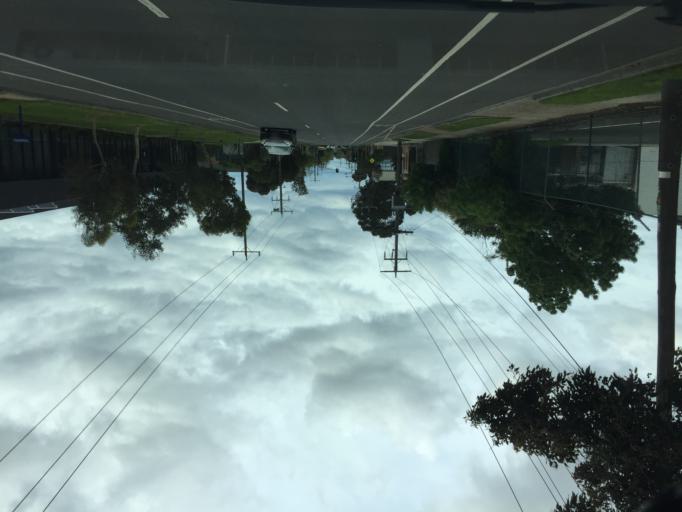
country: AU
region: Victoria
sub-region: Maribyrnong
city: West Footscray
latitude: -37.8026
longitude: 144.8713
